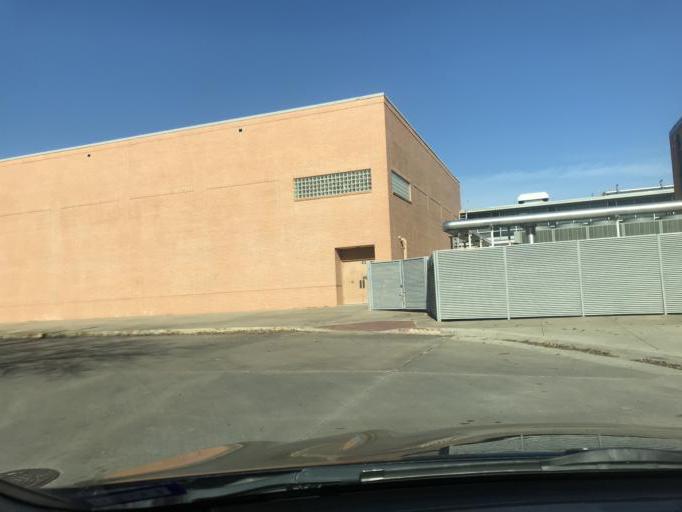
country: US
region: Texas
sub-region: Denton County
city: Denton
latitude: 33.2239
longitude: -97.1444
